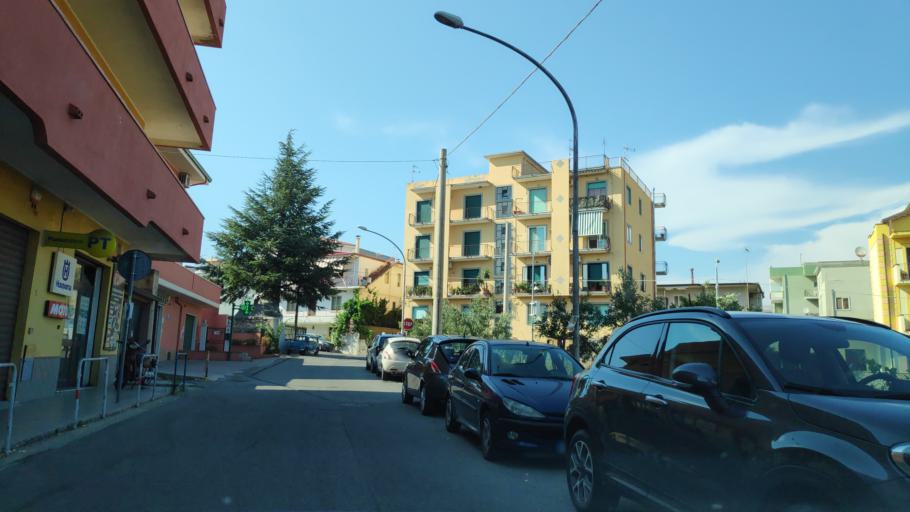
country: IT
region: Calabria
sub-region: Provincia di Catanzaro
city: Soverato Superiore
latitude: 38.6891
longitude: 16.5342
